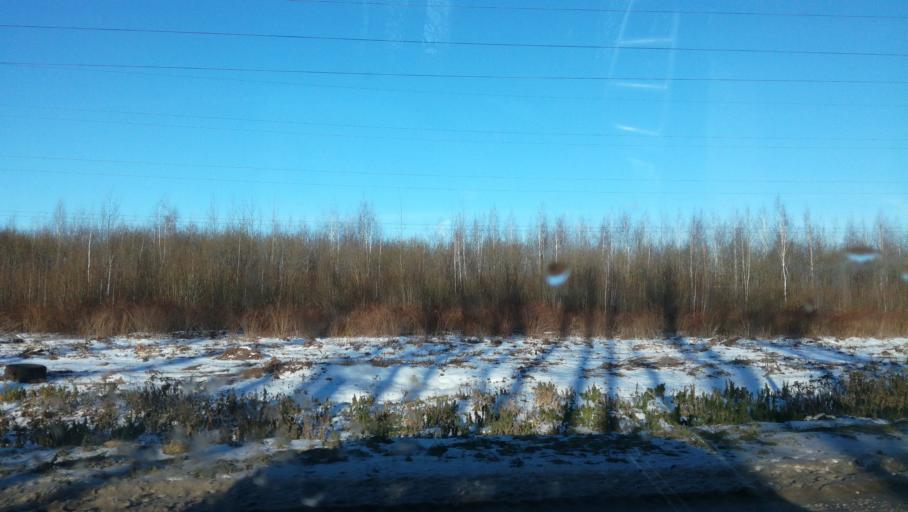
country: RU
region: Tula
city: Kosaya Gora
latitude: 54.1789
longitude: 37.5066
